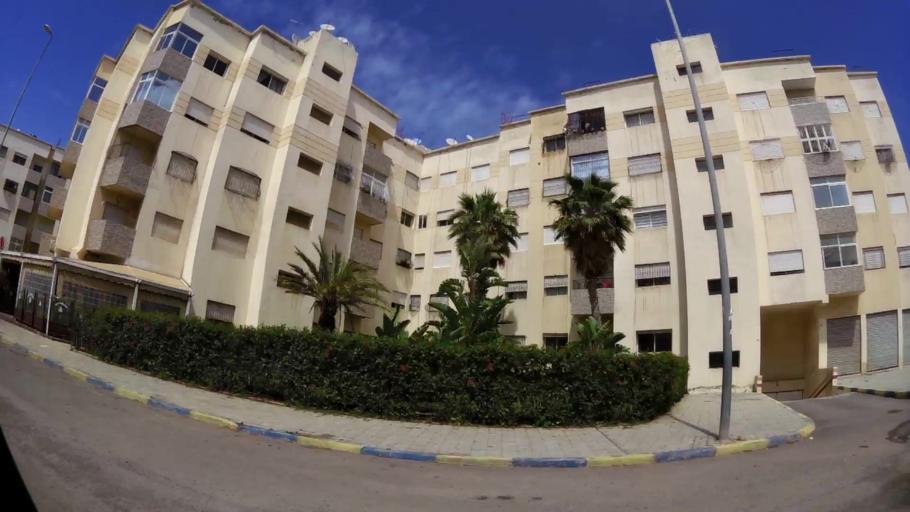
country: MA
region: Grand Casablanca
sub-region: Mediouna
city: Tit Mellil
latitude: 33.6091
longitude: -7.4824
